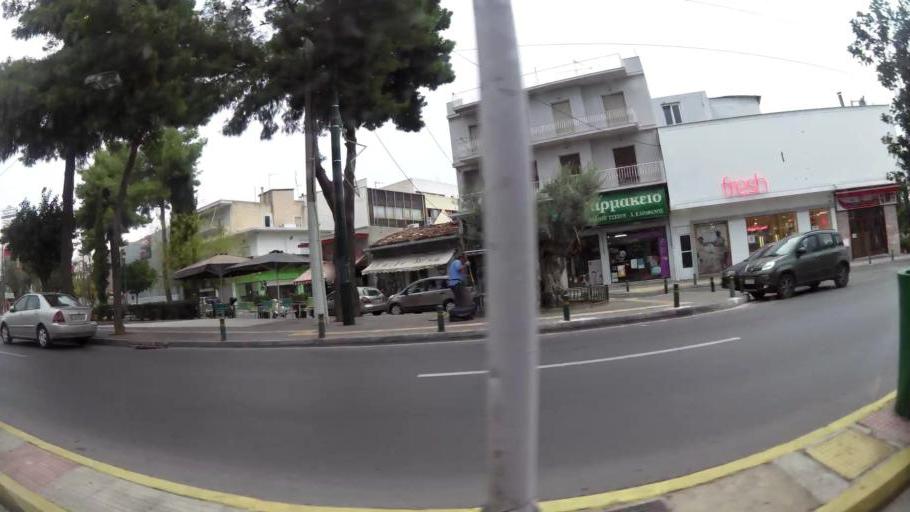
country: GR
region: Attica
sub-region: Nomarchia Athinas
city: Peristeri
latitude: 38.0106
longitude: 23.6975
